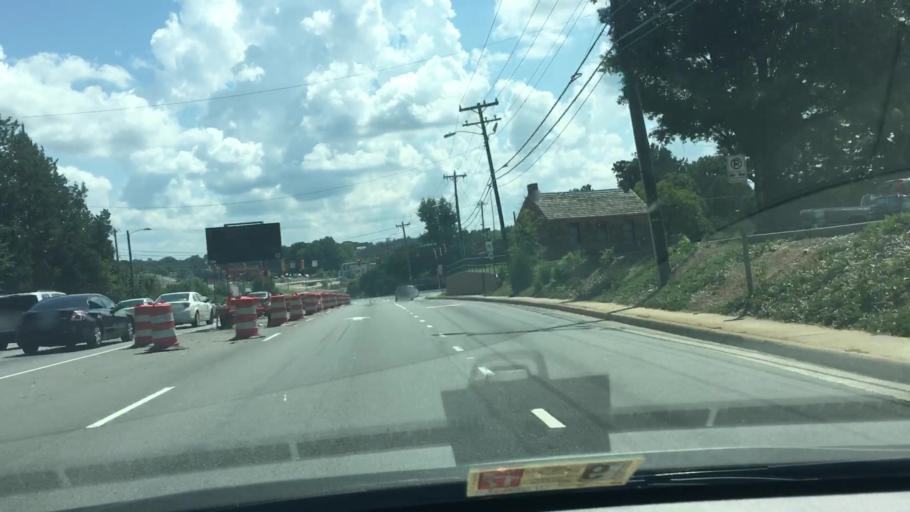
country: US
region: North Carolina
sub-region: Mecklenburg County
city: Charlotte
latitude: 35.2594
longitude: -80.7951
